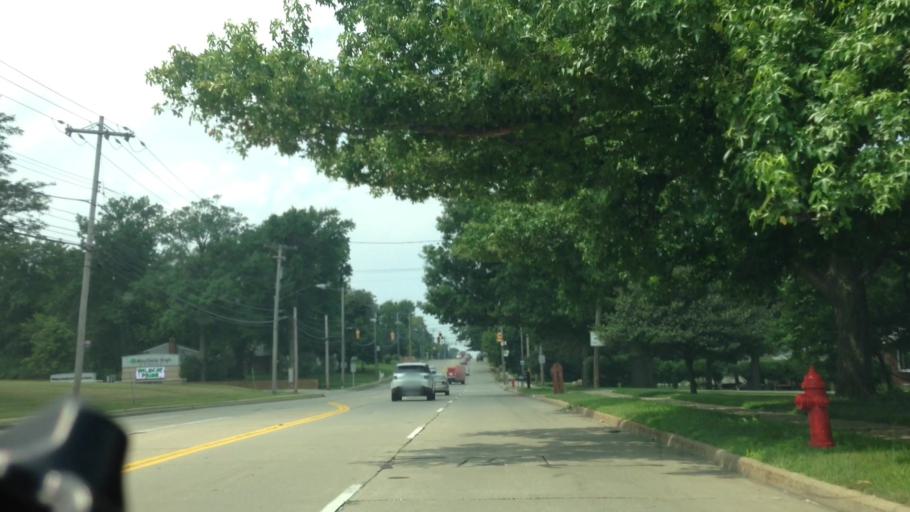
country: US
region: Ohio
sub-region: Cuyahoga County
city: Mayfield Heights
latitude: 41.5390
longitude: -81.4588
